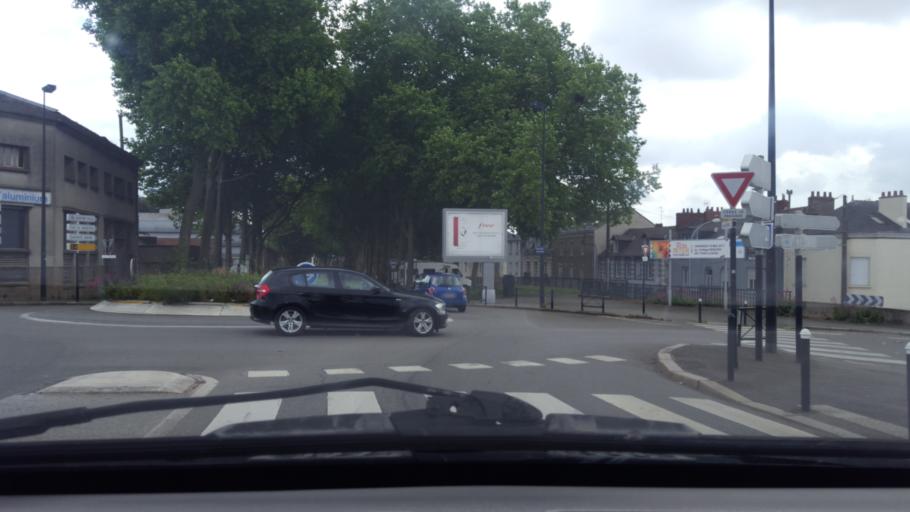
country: FR
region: Pays de la Loire
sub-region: Departement de la Loire-Atlantique
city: Bouguenais
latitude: 47.1984
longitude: -1.5888
